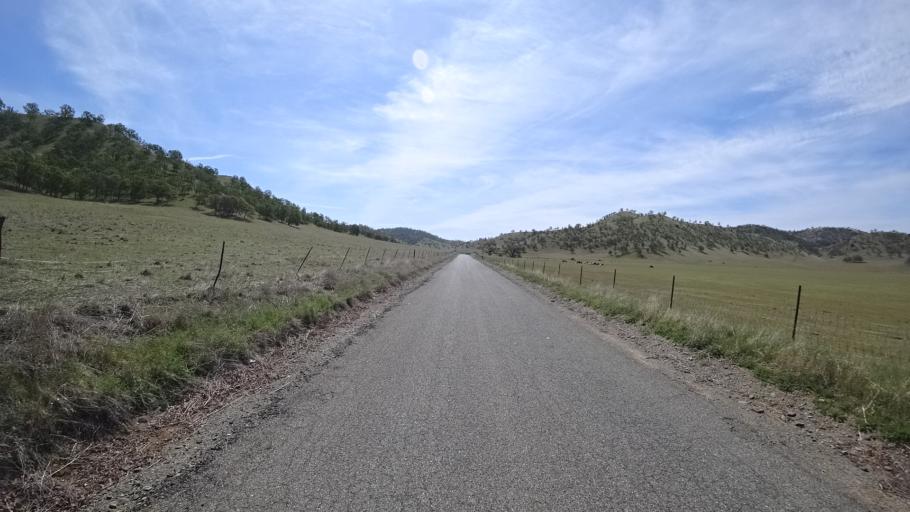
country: US
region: California
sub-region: Glenn County
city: Willows
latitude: 39.5420
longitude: -122.4402
